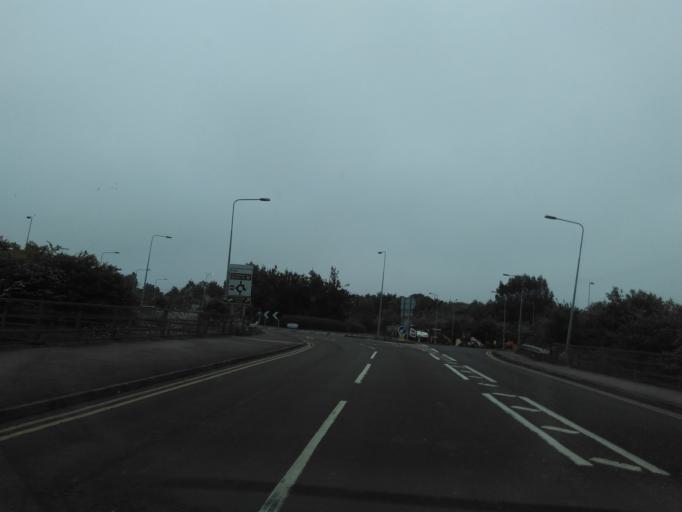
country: GB
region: England
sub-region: Kent
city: Whitstable
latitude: 51.3403
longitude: 1.0206
